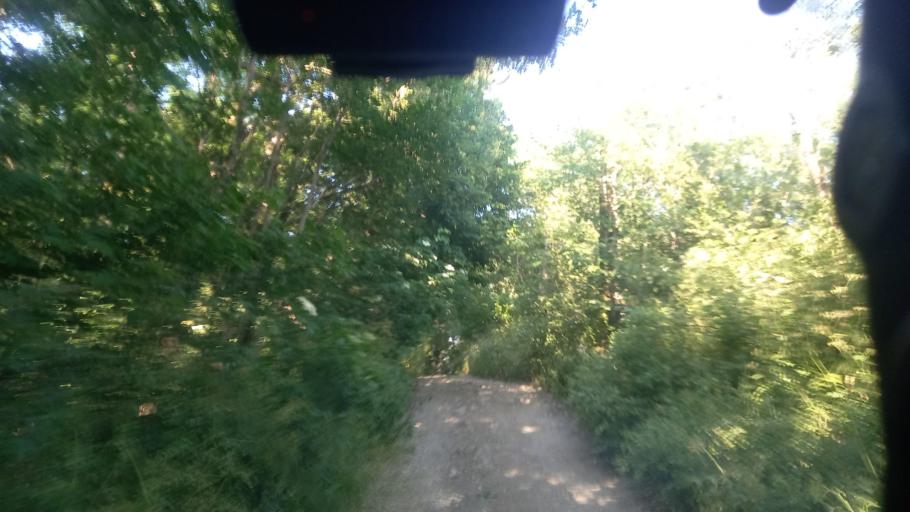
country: RU
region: Krasnodarskiy
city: Gelendzhik
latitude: 44.6187
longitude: 38.1923
